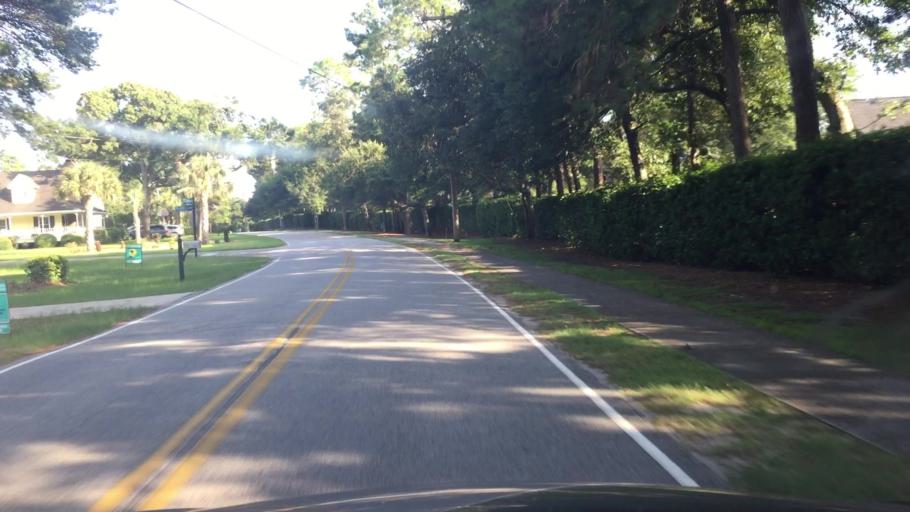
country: US
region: South Carolina
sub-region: Horry County
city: North Myrtle Beach
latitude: 33.8267
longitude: -78.6657
